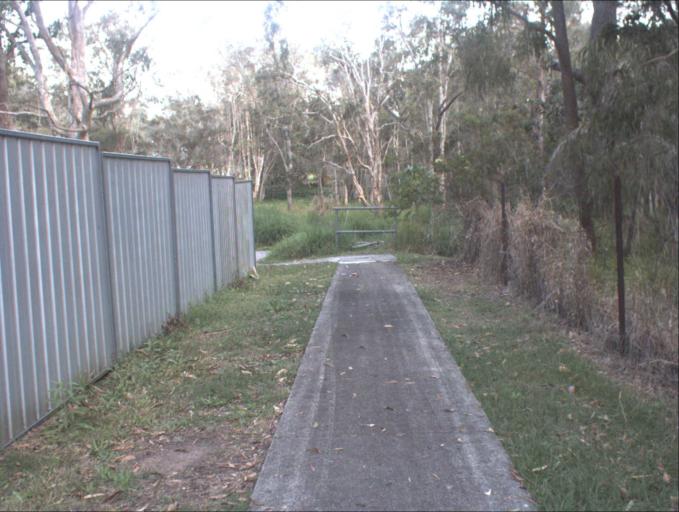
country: AU
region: Queensland
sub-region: Logan
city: Park Ridge South
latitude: -27.7027
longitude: 153.0184
